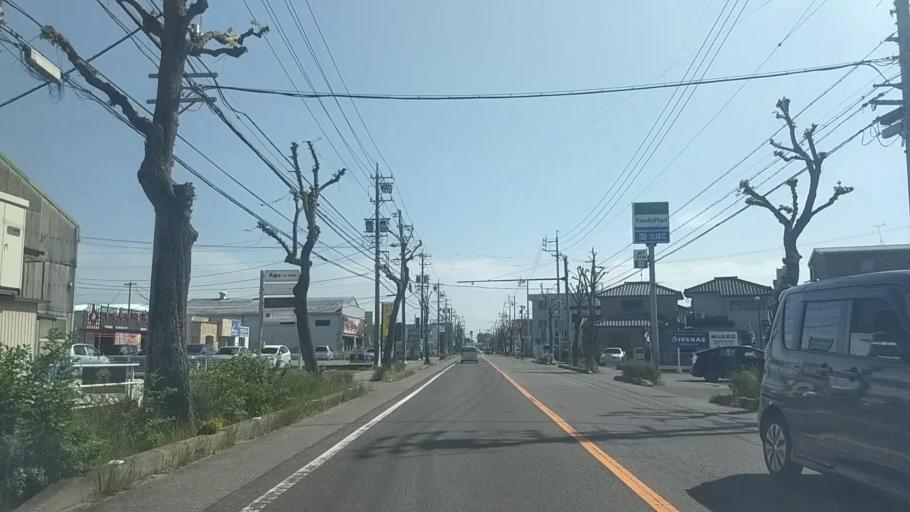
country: JP
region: Aichi
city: Okazaki
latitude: 34.9829
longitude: 137.1394
